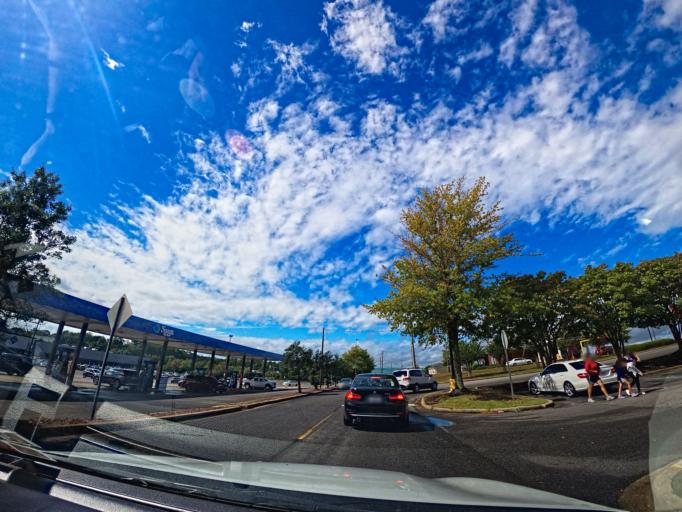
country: US
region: Alabama
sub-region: Tuscaloosa County
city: Tuscaloosa
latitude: 33.1675
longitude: -87.5192
